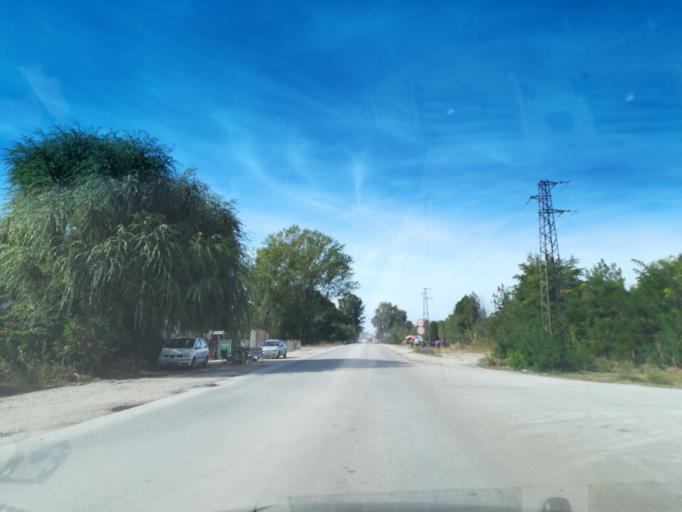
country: BG
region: Plovdiv
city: Stamboliyski
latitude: 42.1192
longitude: 24.5583
